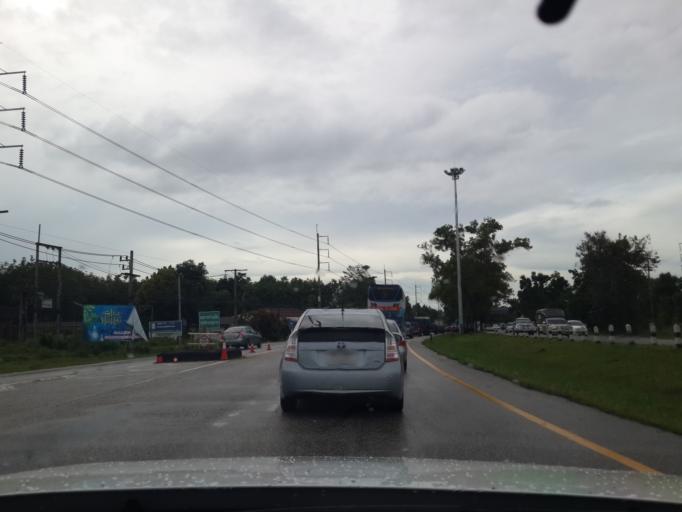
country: TH
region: Songkhla
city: Chana
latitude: 6.9795
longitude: 100.6820
